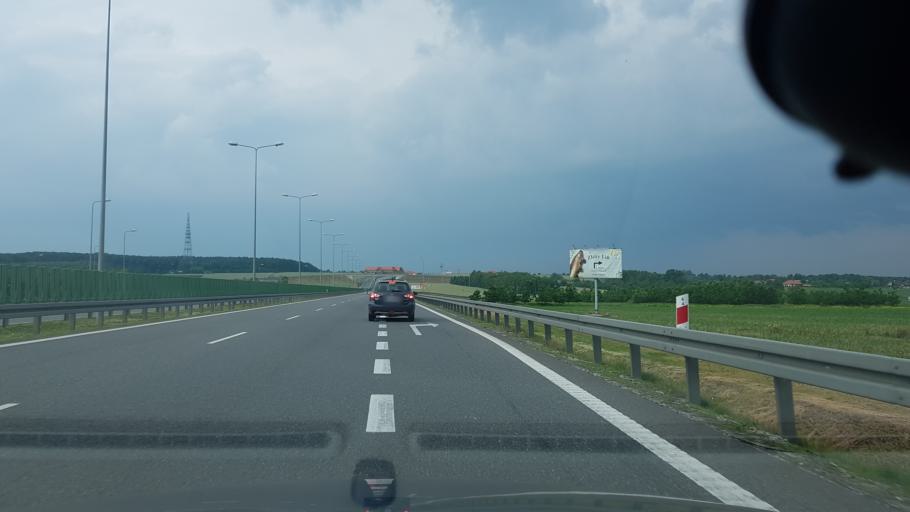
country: PL
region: Masovian Voivodeship
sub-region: Powiat legionowski
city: Serock
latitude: 52.5270
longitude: 21.0577
